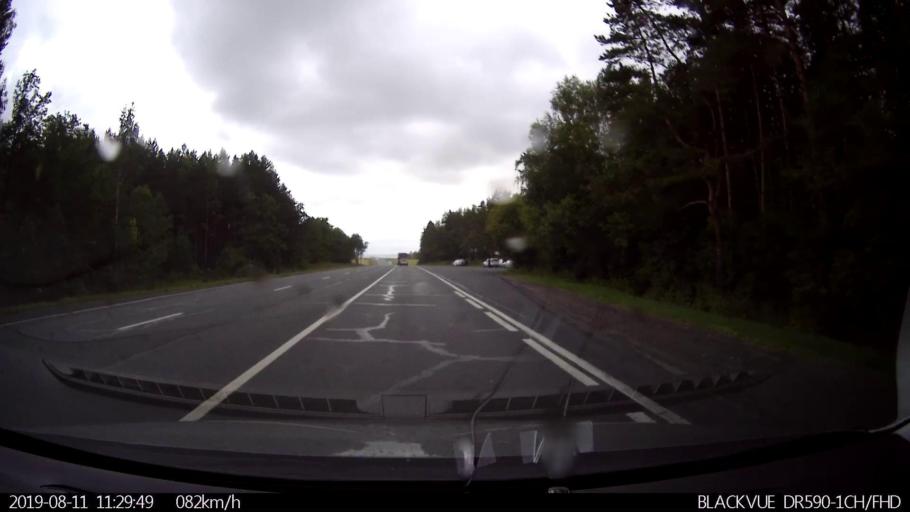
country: RU
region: Ulyanovsk
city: Krasnyy Gulyay
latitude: 54.0656
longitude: 48.2217
